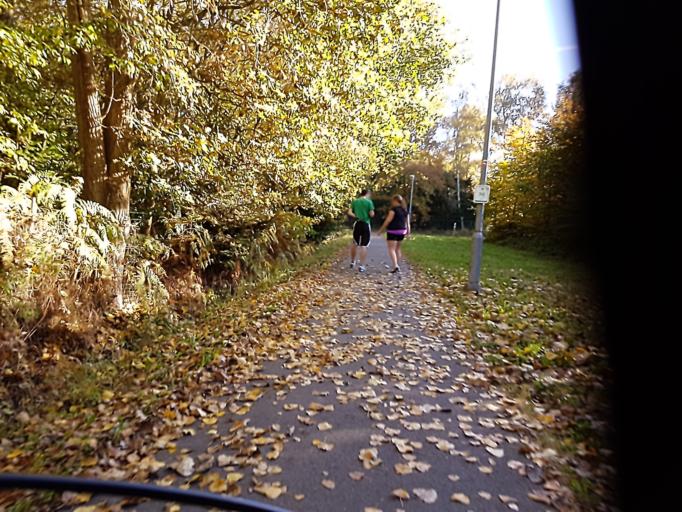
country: BE
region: Flanders
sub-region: Provincie Antwerpen
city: Sint-Katelijne-Waver
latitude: 51.0662
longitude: 4.5724
